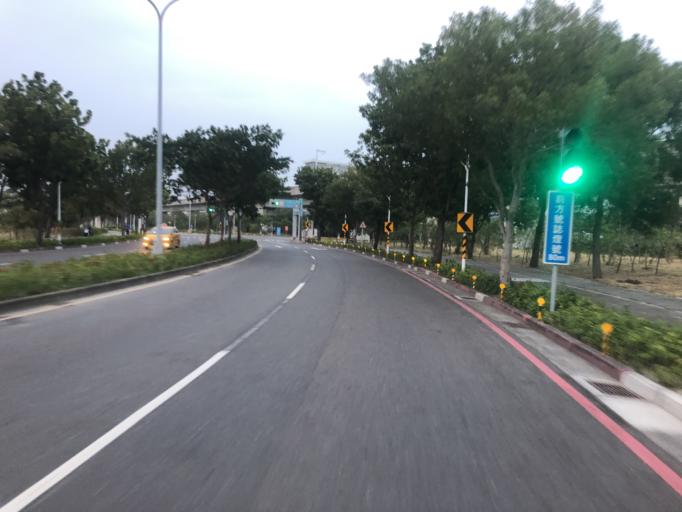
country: TW
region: Taiwan
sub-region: Tainan
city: Tainan
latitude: 23.0865
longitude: 120.2861
